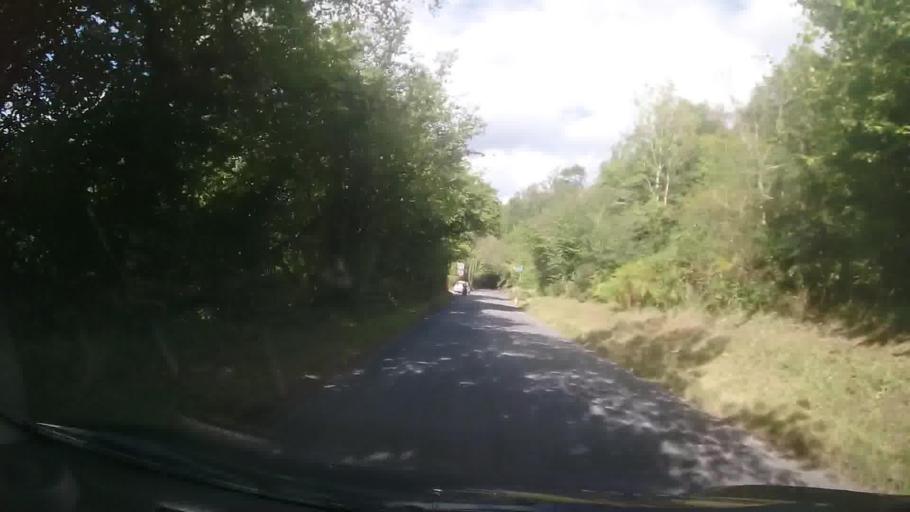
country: GB
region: Wales
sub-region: Merthyr Tydfil County Borough
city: Merthyr Tydfil
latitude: 51.7852
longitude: -3.3629
